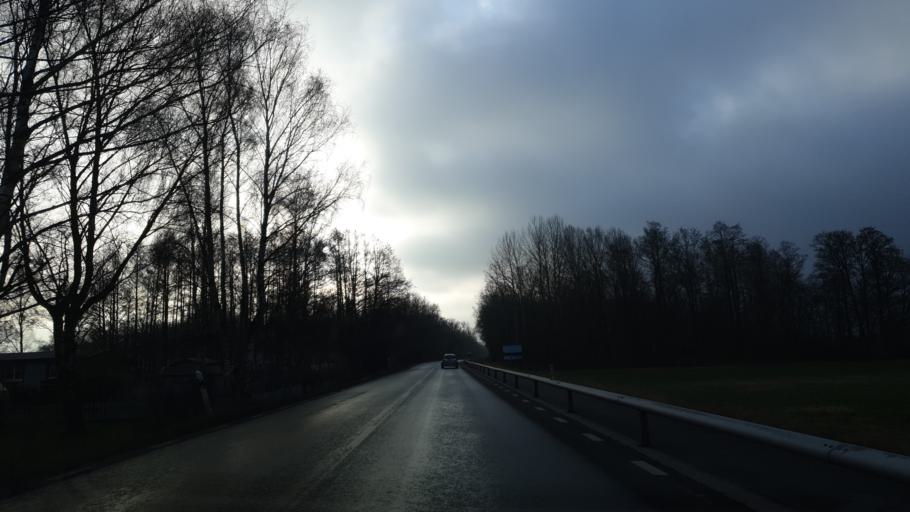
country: SE
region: Blekinge
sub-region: Karlshamns Kommun
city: Morrum
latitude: 56.1338
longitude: 14.6723
